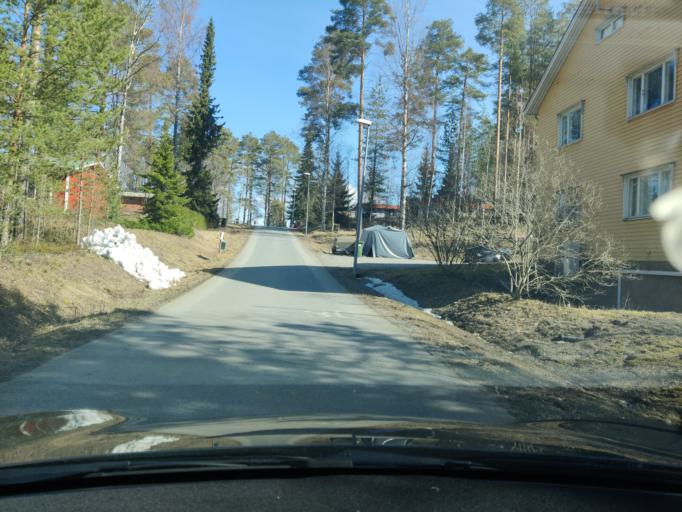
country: FI
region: Northern Savo
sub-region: Kuopio
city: Vehmersalmi
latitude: 62.7625
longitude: 28.0258
